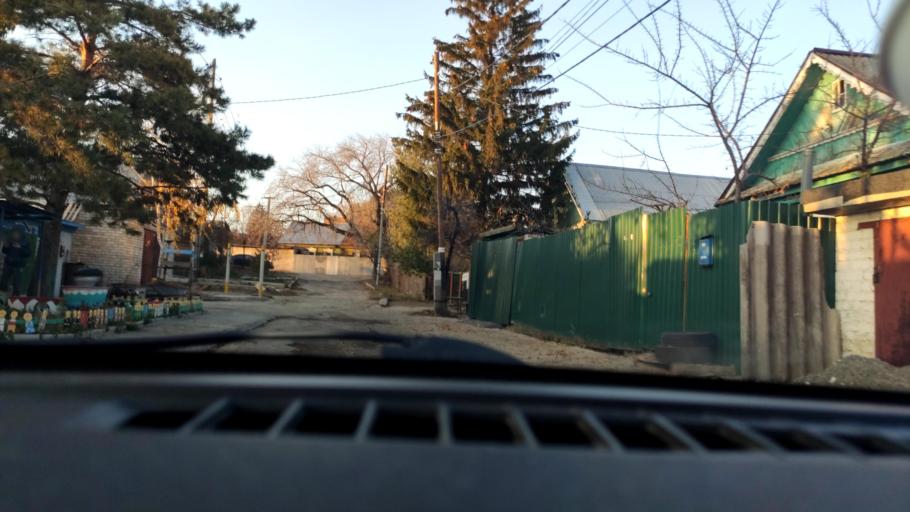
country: RU
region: Samara
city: Samara
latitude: 53.1810
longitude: 50.1900
